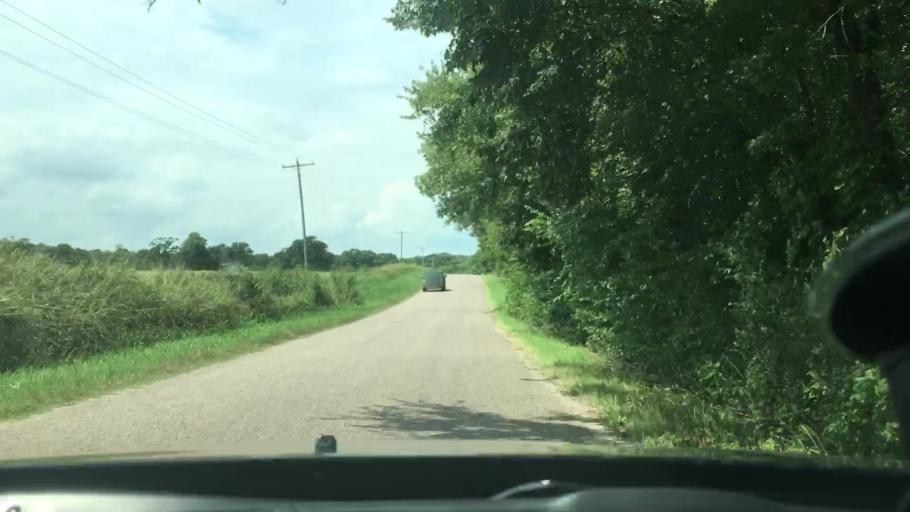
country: US
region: Oklahoma
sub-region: Carter County
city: Dickson
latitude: 34.2272
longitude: -96.8985
